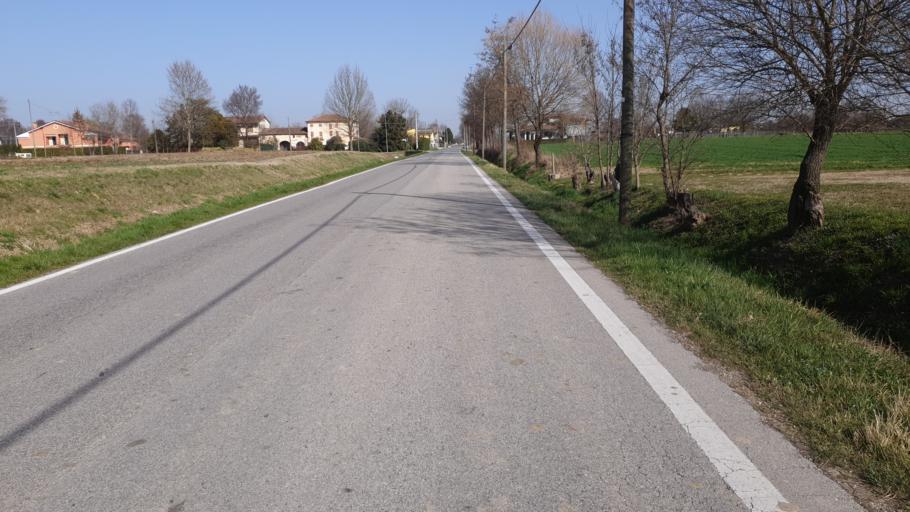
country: IT
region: Veneto
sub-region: Provincia di Padova
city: Cavino
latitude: 45.5037
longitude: 11.8887
